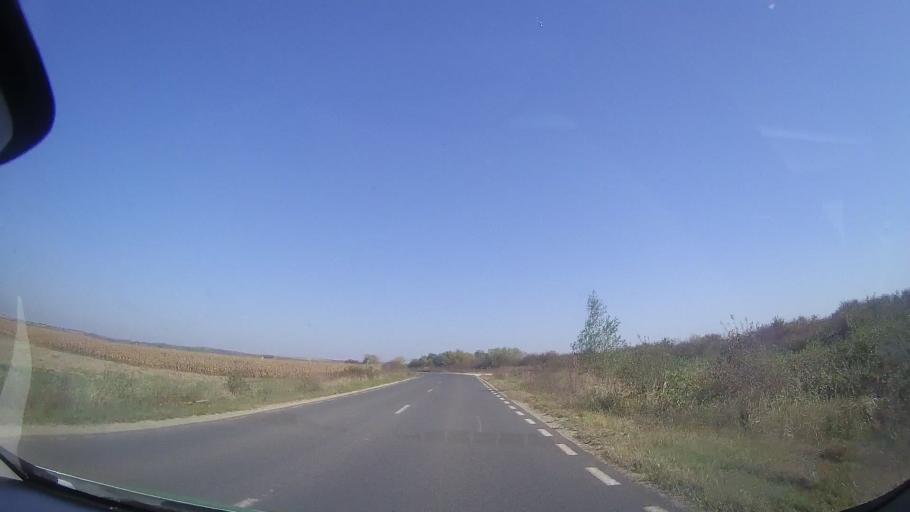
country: RO
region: Timis
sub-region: Comuna Balint
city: Balint
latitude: 45.7918
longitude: 21.8584
